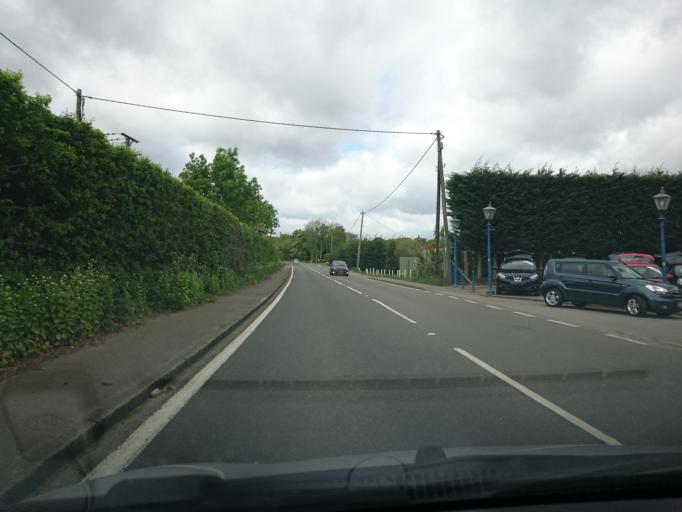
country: GB
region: England
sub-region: Surrey
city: Pirbright
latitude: 51.2648
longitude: -0.6322
